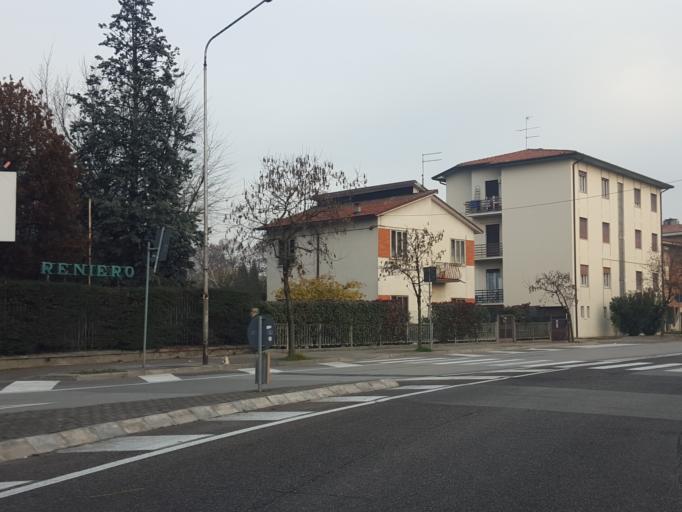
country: IT
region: Veneto
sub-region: Provincia di Vicenza
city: Vicenza
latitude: 45.5477
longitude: 11.5173
